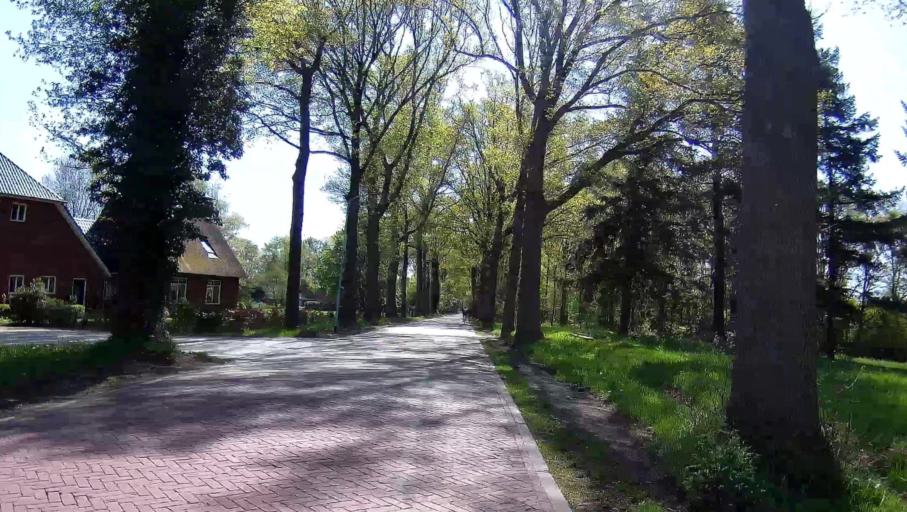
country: NL
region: Drenthe
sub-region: Gemeente Borger-Odoorn
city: Borger
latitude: 52.9692
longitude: 6.8161
